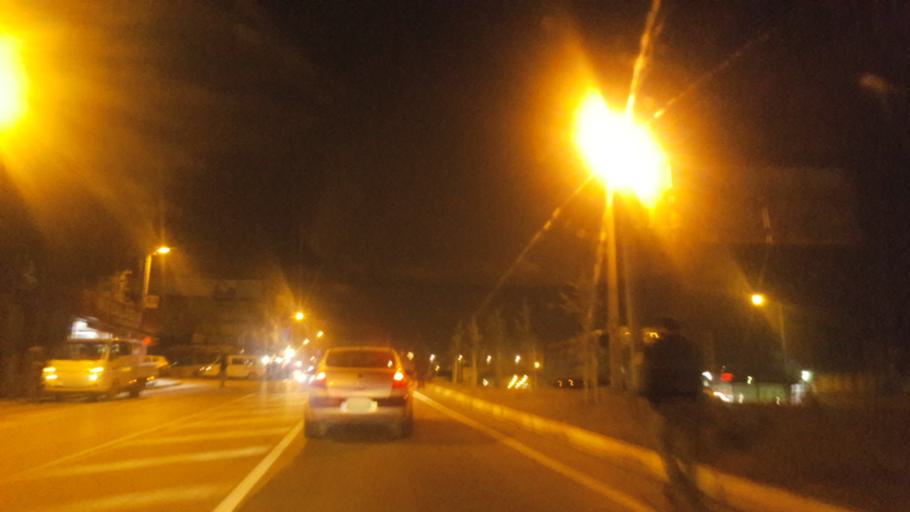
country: TR
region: Kocaeli
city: Tavsanli
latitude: 40.7889
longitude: 29.5318
